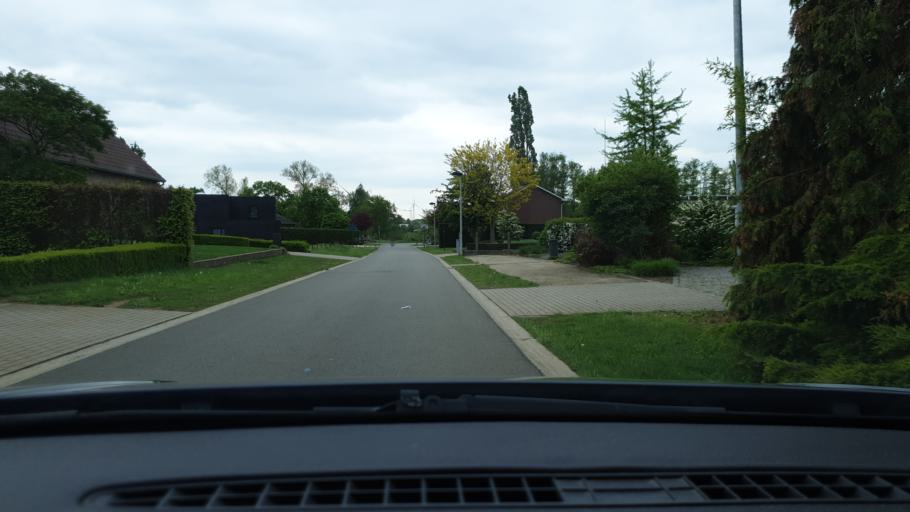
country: BE
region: Flanders
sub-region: Provincie Antwerpen
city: Meerhout
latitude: 51.1246
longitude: 5.0917
